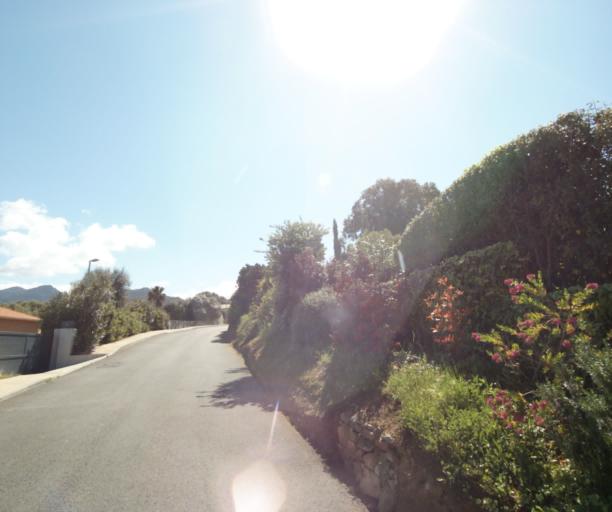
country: FR
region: Corsica
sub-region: Departement de la Corse-du-Sud
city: Propriano
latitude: 41.6750
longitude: 8.9098
